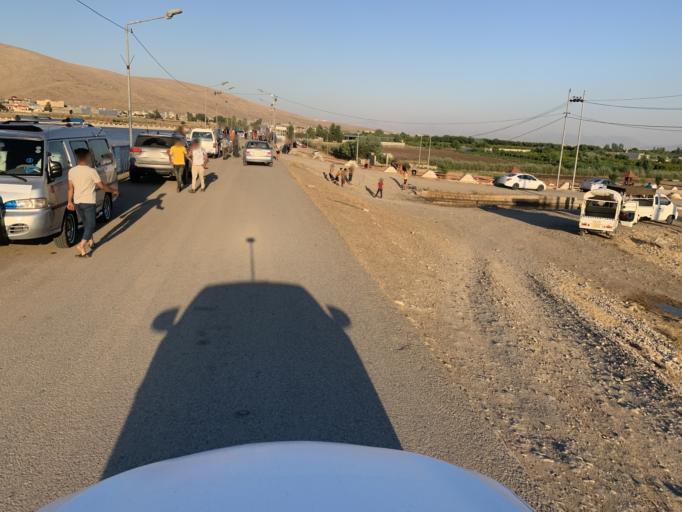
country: IQ
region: As Sulaymaniyah
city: Raniye
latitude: 36.2727
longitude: 44.7510
